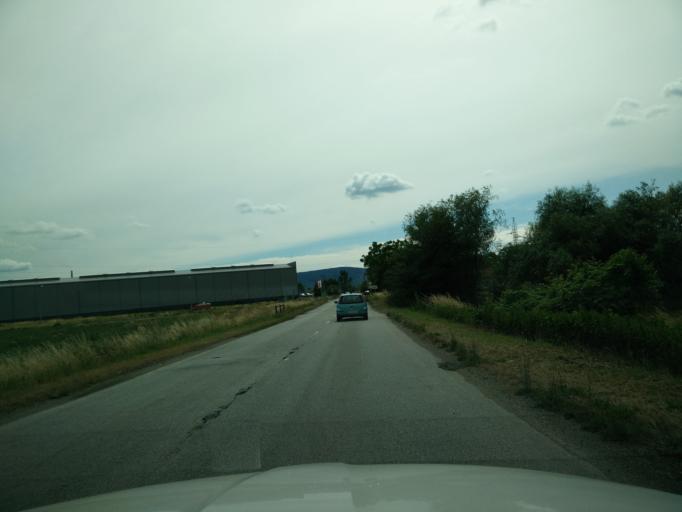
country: SK
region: Nitriansky
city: Novaky
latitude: 48.7276
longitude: 18.5556
